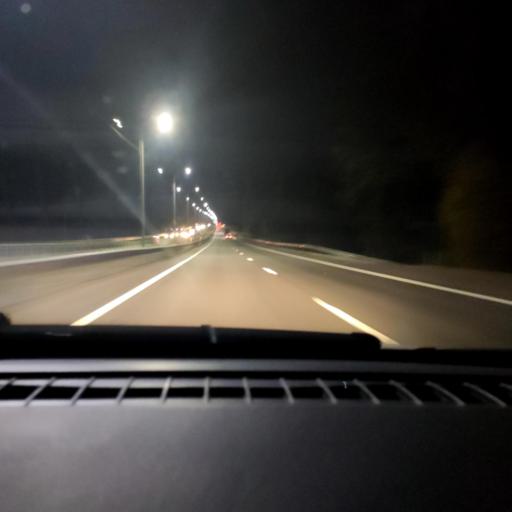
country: RU
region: Voronezj
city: Ramon'
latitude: 51.8686
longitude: 39.2164
